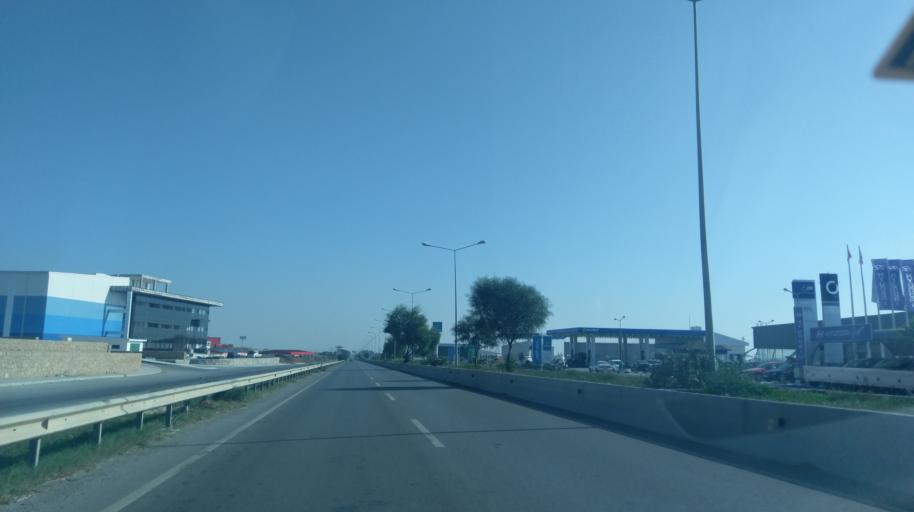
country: CY
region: Lefkosia
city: Nicosia
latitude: 35.2159
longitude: 33.4278
